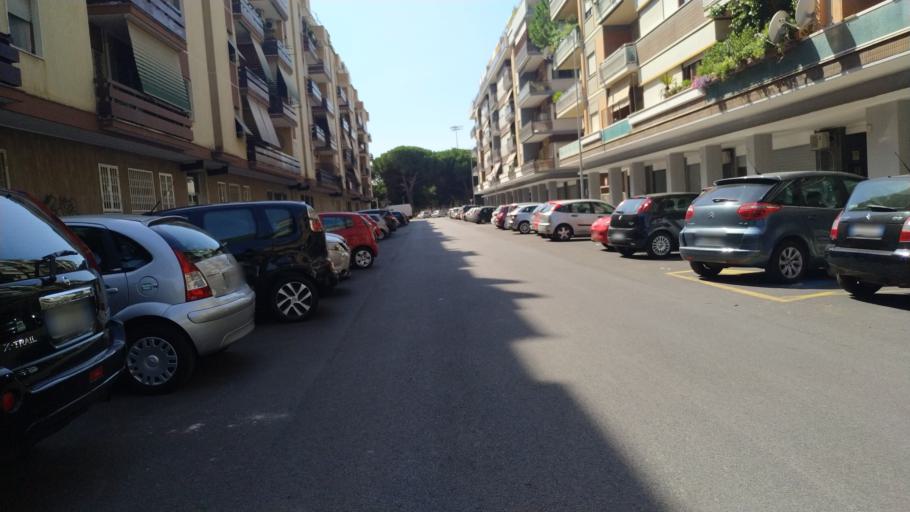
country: IT
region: Latium
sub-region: Citta metropolitana di Roma Capitale
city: Lido di Ostia
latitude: 41.7335
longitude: 12.3023
